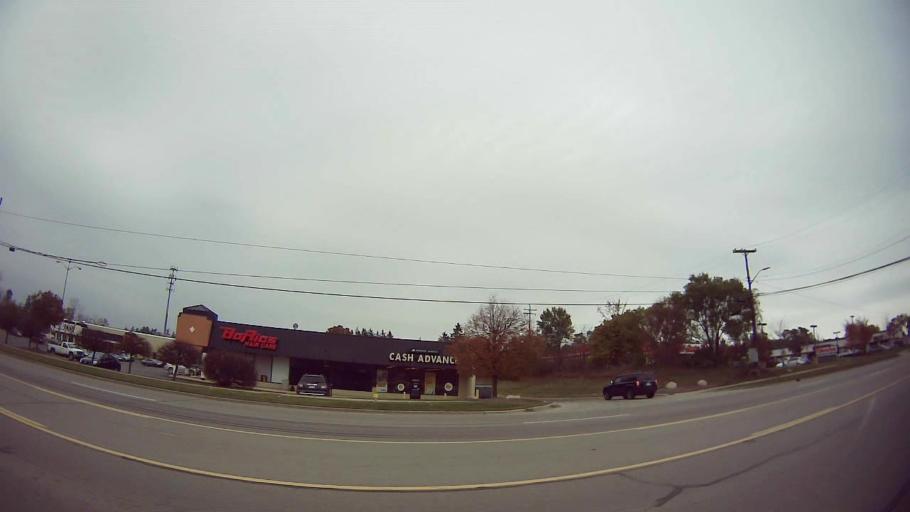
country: US
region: Michigan
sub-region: Oakland County
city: Waterford
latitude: 42.7005
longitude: -83.4015
